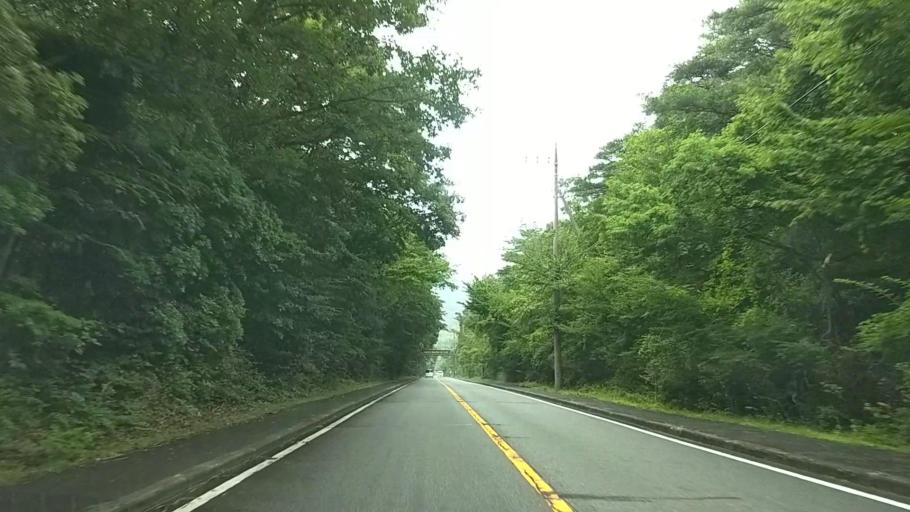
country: JP
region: Yamanashi
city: Fujikawaguchiko
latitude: 35.4661
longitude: 138.6014
